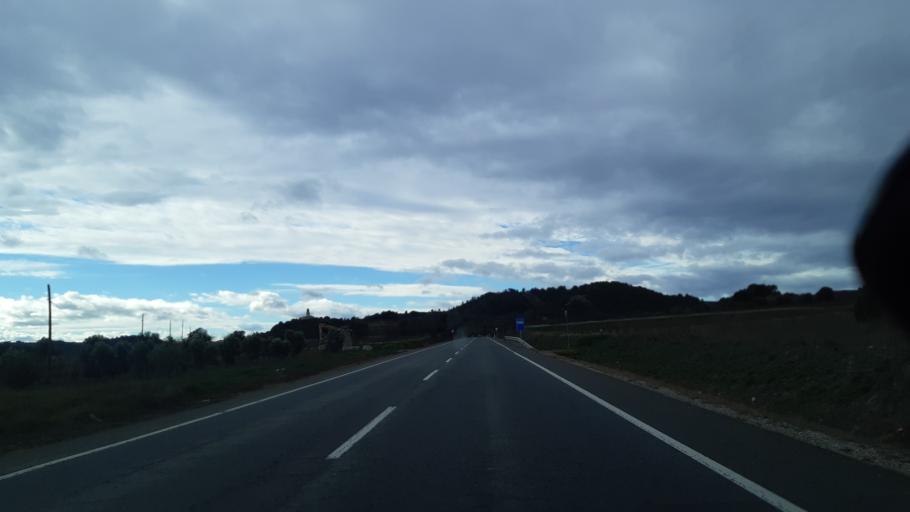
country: ES
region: Catalonia
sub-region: Provincia de Tarragona
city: Gandesa
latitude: 41.0849
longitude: 0.4963
